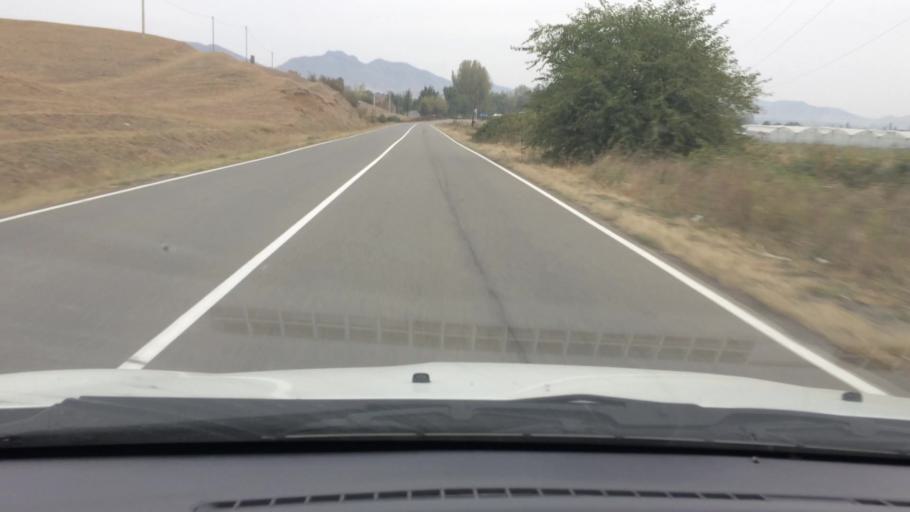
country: AM
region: Tavush
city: Bagratashen
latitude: 41.2884
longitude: 44.7889
